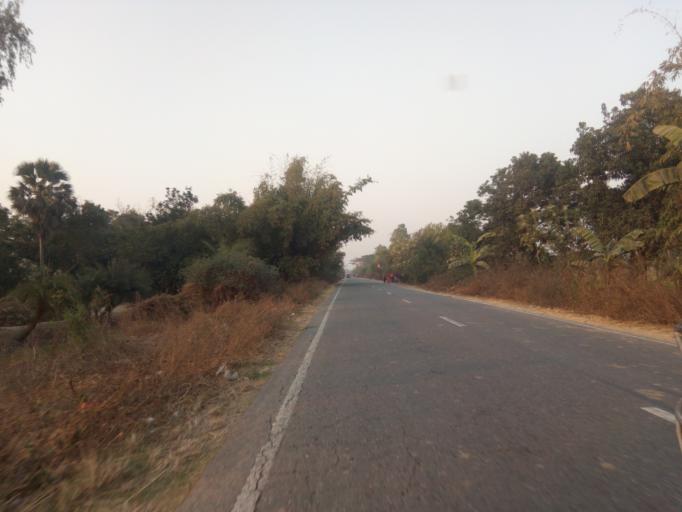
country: BD
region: Rajshahi
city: Bogra
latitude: 24.6031
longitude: 89.2397
